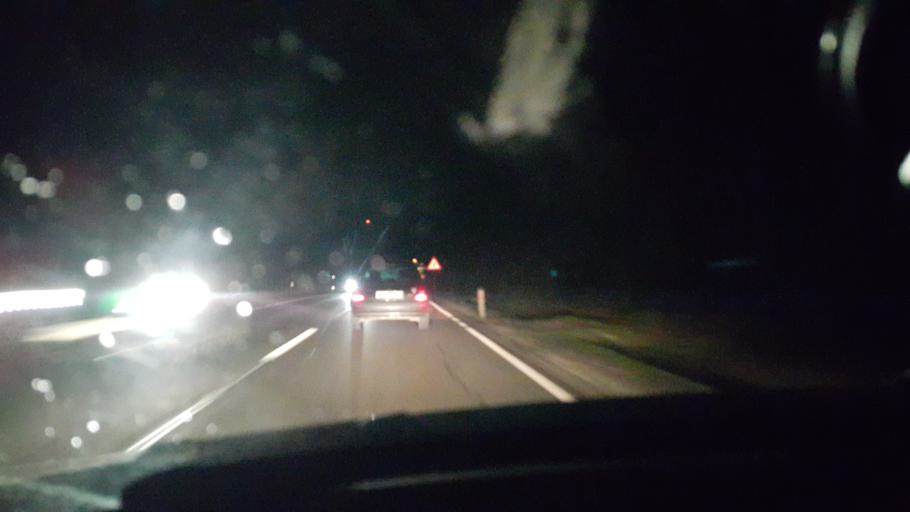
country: SI
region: Kidricevo
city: Kidricevo
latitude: 46.4121
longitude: 15.8037
